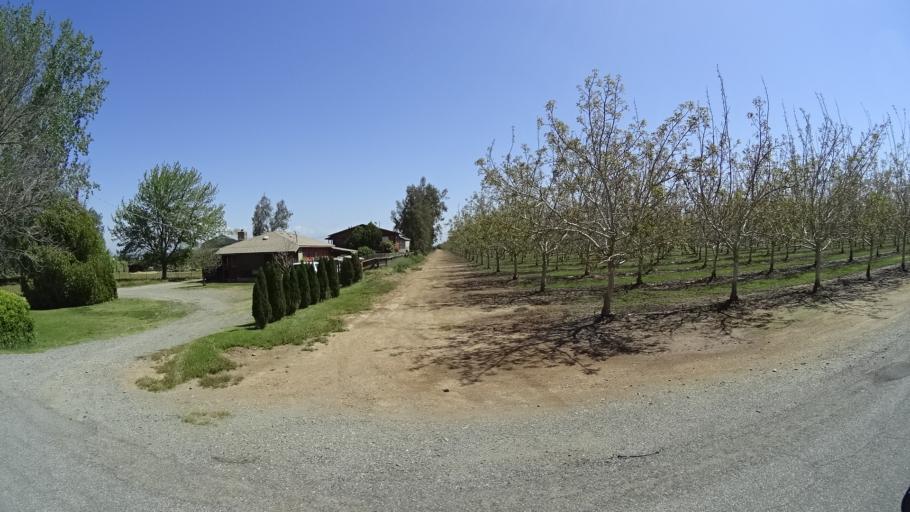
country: US
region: California
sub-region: Glenn County
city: Orland
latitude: 39.7708
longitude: -122.1783
